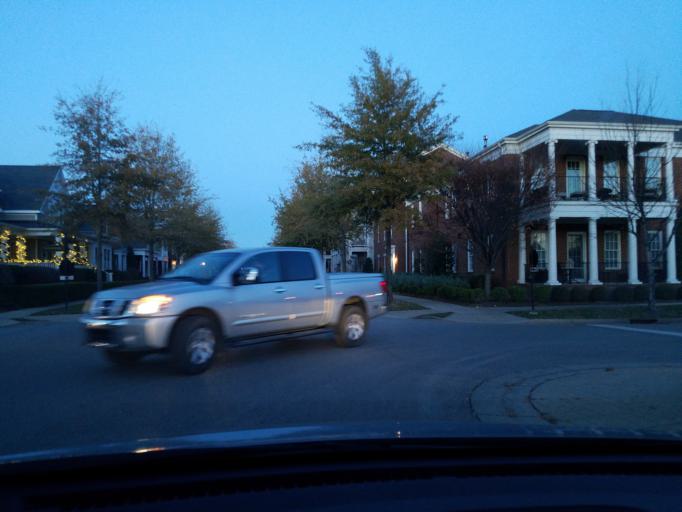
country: US
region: Kentucky
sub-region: Jefferson County
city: Worthington
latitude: 38.3228
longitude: -85.5687
